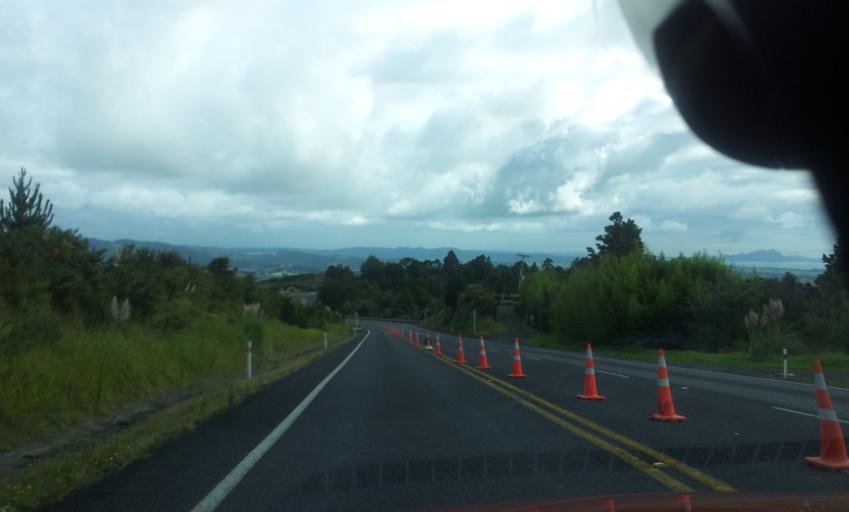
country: NZ
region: Northland
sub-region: Whangarei
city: Ruakaka
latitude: -36.0596
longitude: 174.4272
